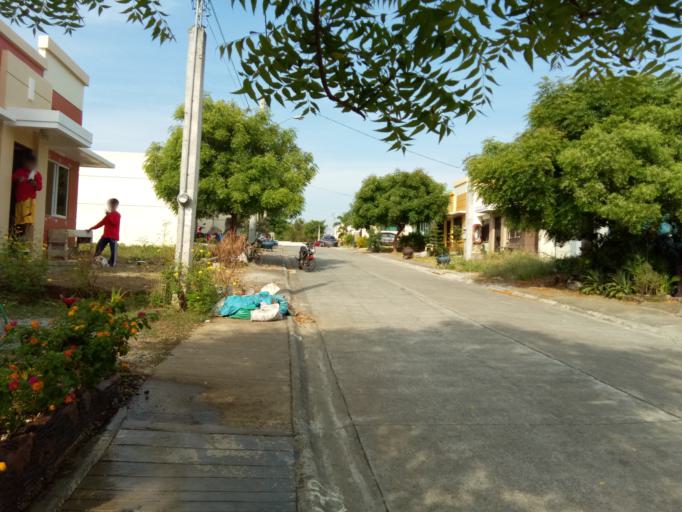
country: PH
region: Calabarzon
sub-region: Province of Cavite
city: Bulihan
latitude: 14.2787
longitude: 120.9738
